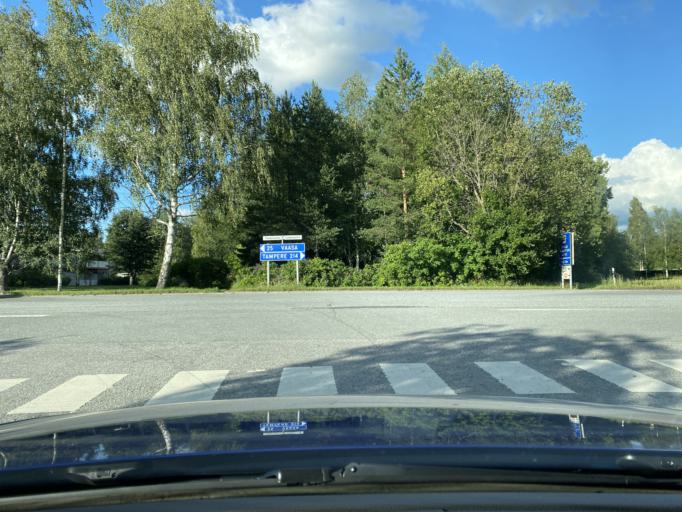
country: FI
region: Ostrobothnia
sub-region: Kyroenmaa
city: Laihia
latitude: 62.9781
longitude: 22.0130
